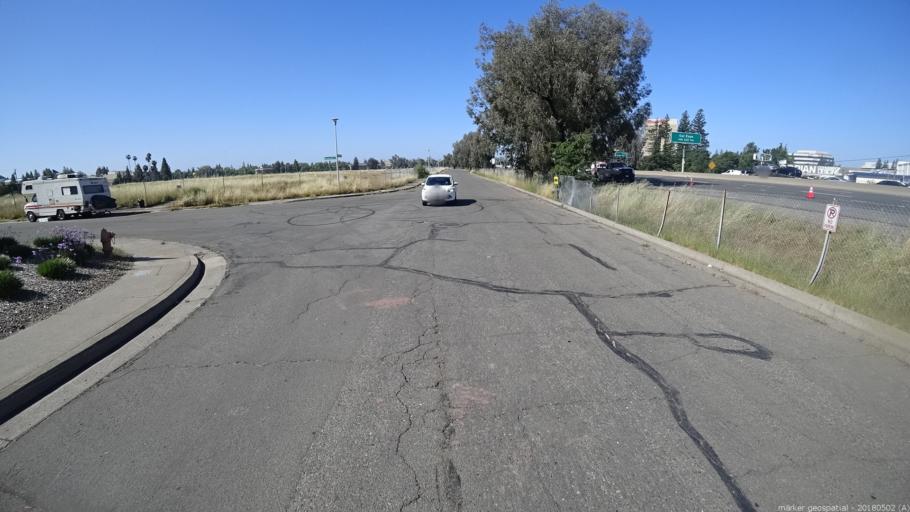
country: US
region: California
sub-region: Sacramento County
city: Arden-Arcade
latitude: 38.6075
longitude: -121.4302
